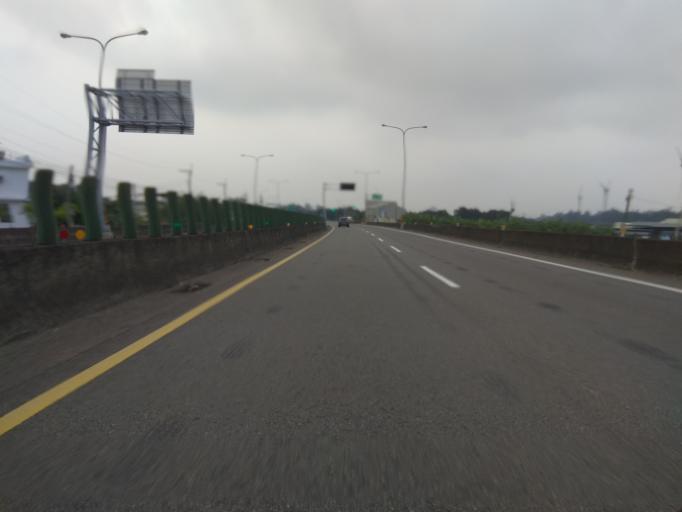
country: TW
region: Taiwan
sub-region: Hsinchu
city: Hsinchu
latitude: 24.7140
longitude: 120.8672
